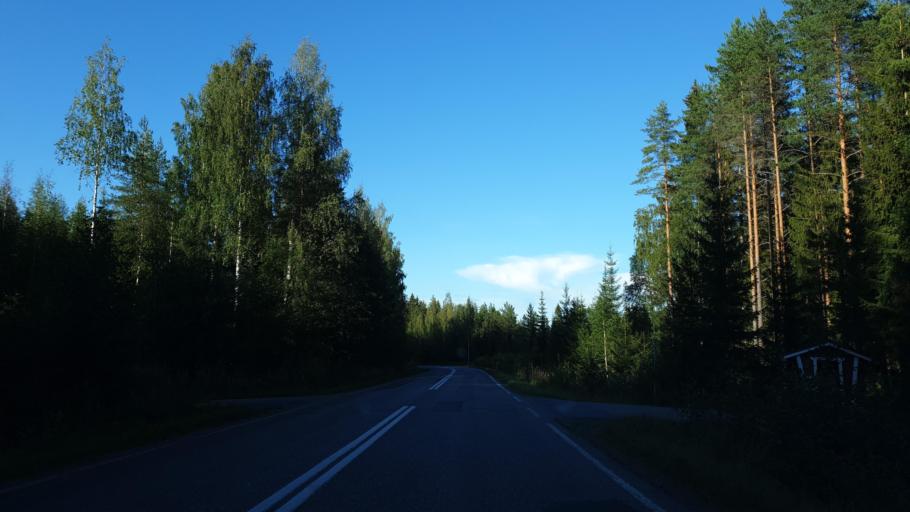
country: FI
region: Northern Savo
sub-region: Koillis-Savo
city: Juankoski
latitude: 63.1008
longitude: 28.4361
